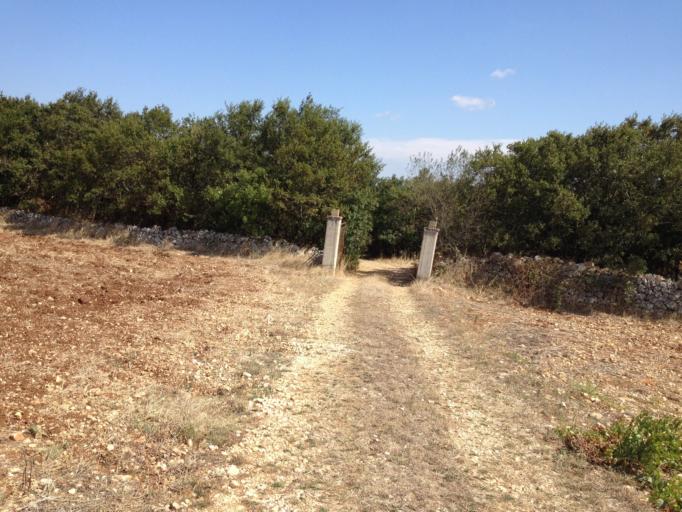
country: IT
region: Apulia
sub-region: Provincia di Bari
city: Gioia del Colle
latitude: 40.8213
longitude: 16.9988
